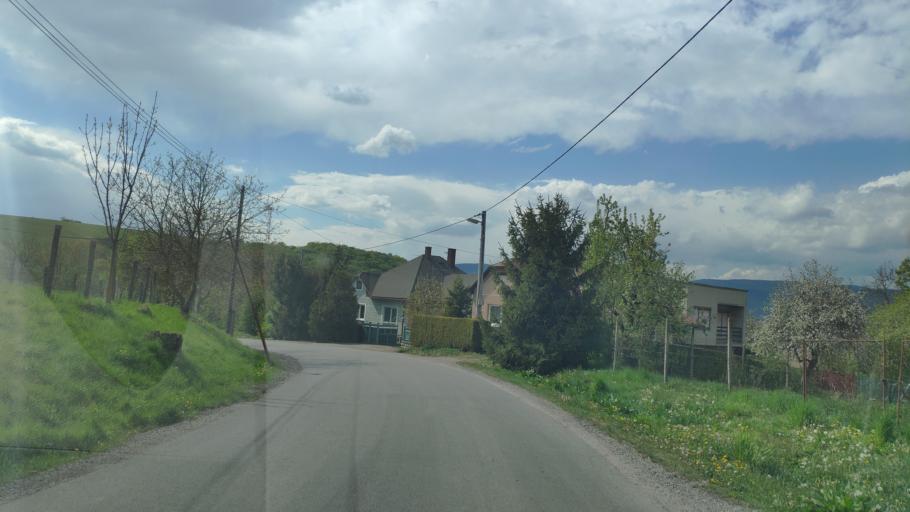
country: SK
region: Kosicky
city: Moldava nad Bodvou
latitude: 48.5856
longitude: 20.9189
